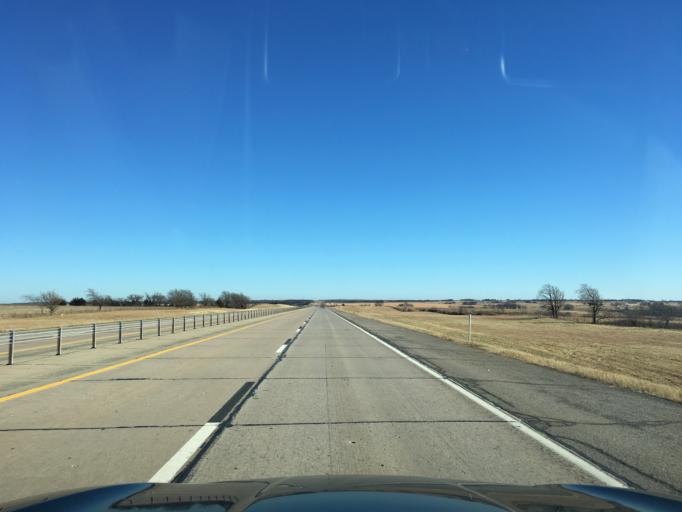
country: US
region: Oklahoma
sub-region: Pawnee County
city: Pawnee
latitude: 36.2253
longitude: -96.8683
